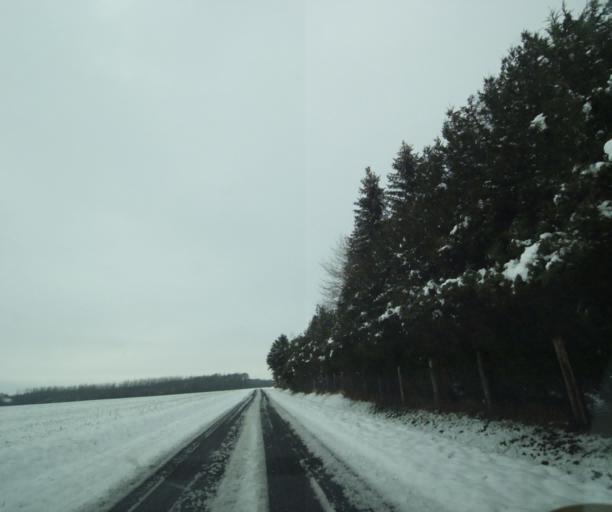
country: FR
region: Champagne-Ardenne
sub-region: Departement de la Haute-Marne
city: Montier-en-Der
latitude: 48.4810
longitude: 4.6722
